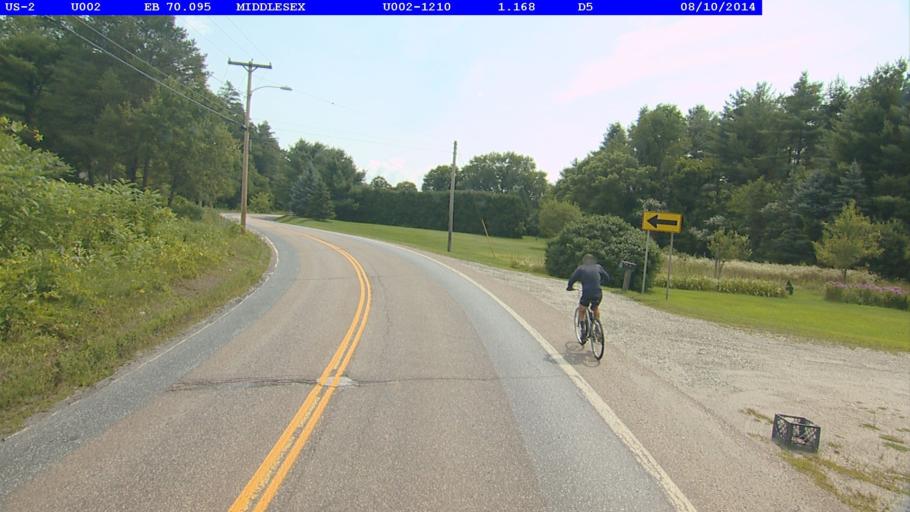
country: US
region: Vermont
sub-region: Washington County
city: Waterbury
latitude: 44.2938
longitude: -72.6817
